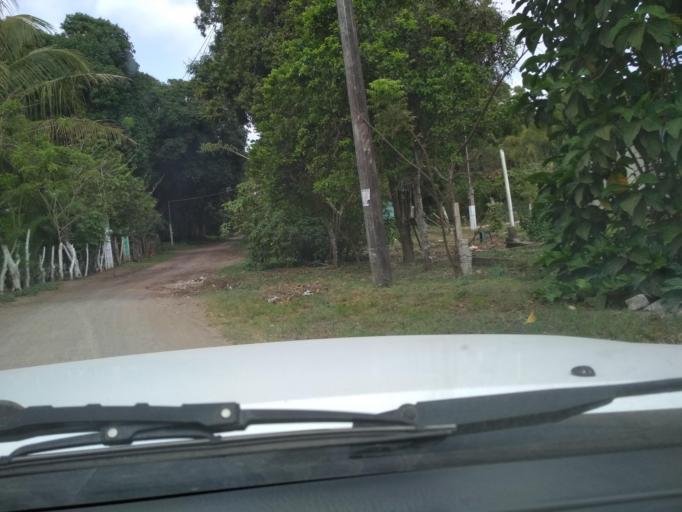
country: MX
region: Veracruz
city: El Tejar
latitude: 19.0727
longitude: -96.1691
